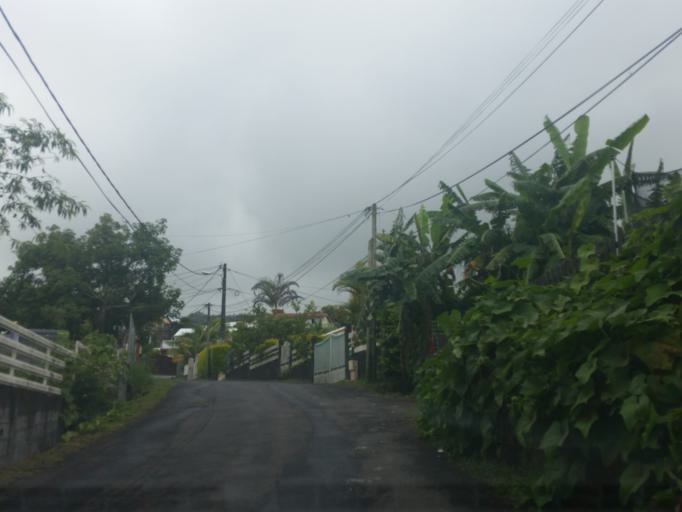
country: RE
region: Reunion
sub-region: Reunion
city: Le Tampon
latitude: -21.2376
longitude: 55.5193
